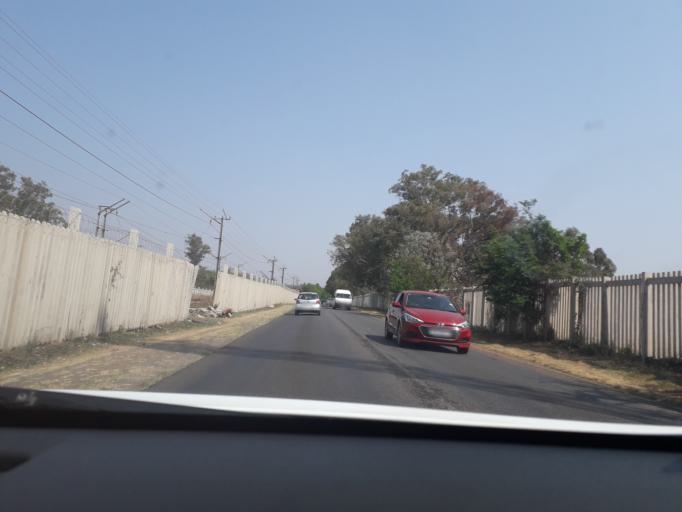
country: ZA
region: Gauteng
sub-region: City of Tshwane Metropolitan Municipality
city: Centurion
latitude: -25.8866
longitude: 28.2240
